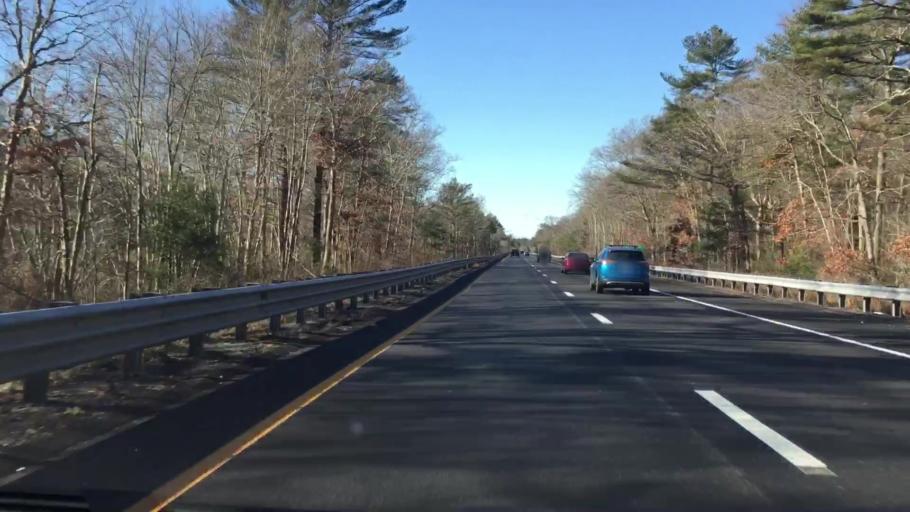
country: US
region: Massachusetts
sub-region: Plymouth County
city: West Wareham
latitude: 41.8104
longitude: -70.7817
